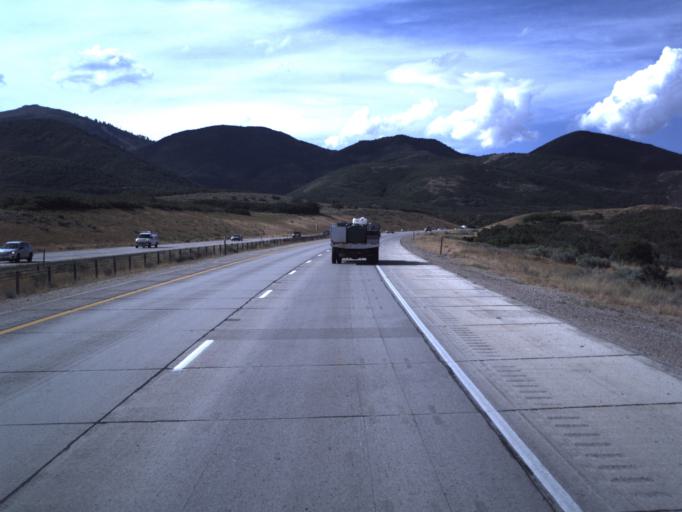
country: US
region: Utah
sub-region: Wasatch County
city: Heber
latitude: 40.5745
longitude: -111.4338
